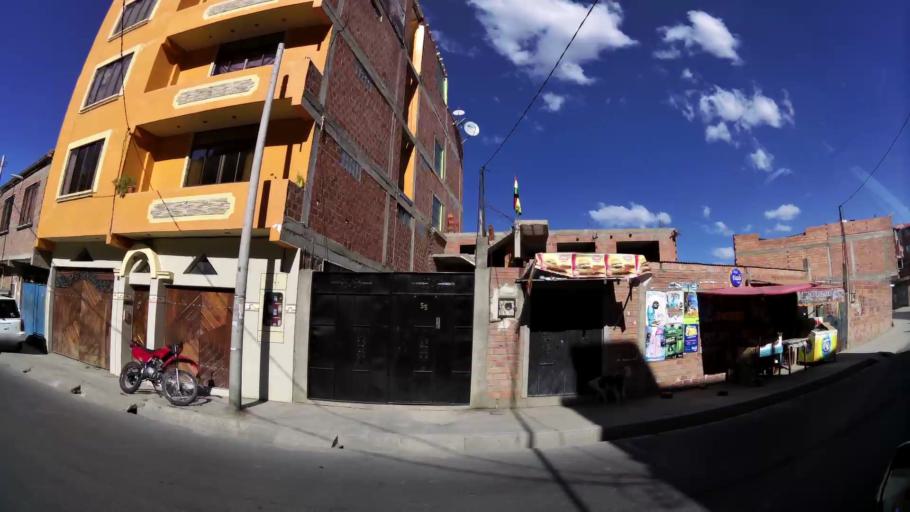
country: BO
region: La Paz
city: La Paz
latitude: -16.5183
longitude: -68.1235
